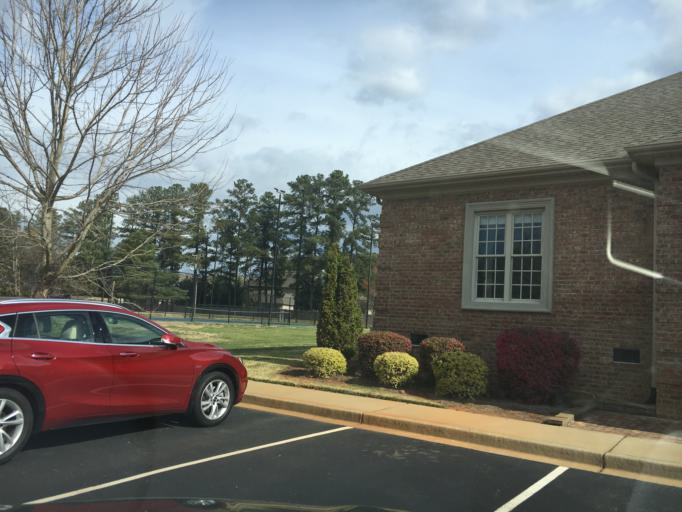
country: US
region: South Carolina
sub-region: Greenville County
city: Taylors
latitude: 34.8643
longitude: -82.2733
